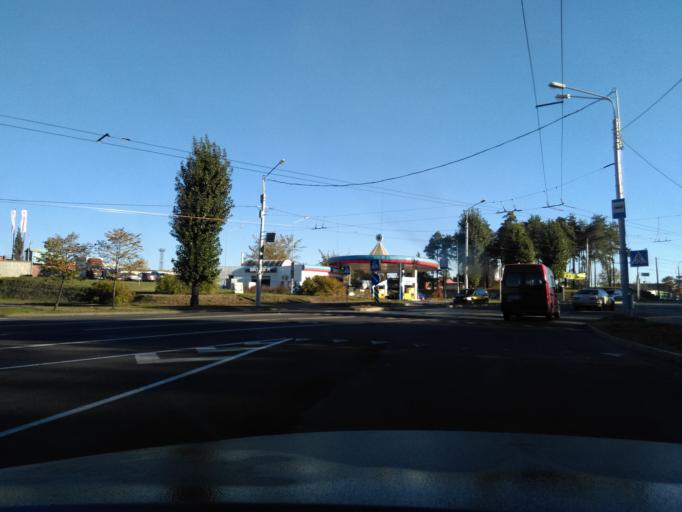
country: BY
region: Minsk
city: Minsk
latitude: 53.8855
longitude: 27.6227
